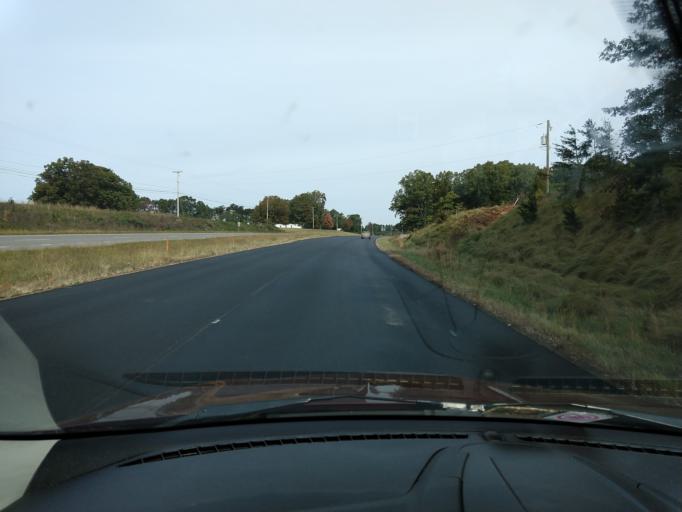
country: US
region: Virginia
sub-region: Pittsylvania County
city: Chatham
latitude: 36.8719
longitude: -79.4090
